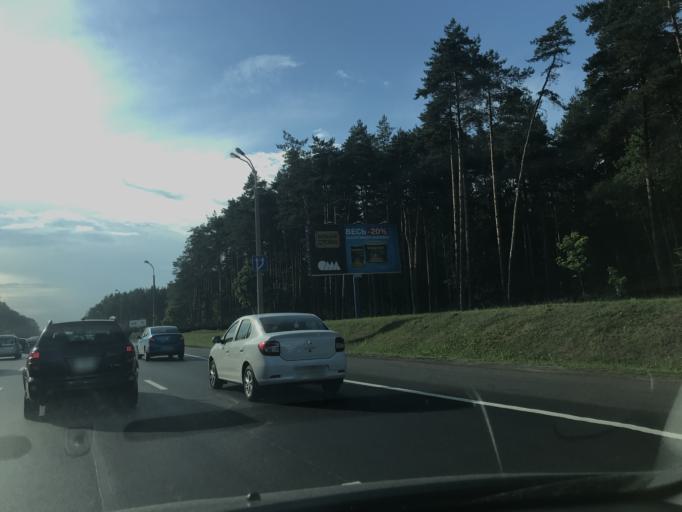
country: BY
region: Minsk
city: Borovlyany
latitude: 53.9541
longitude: 27.6428
